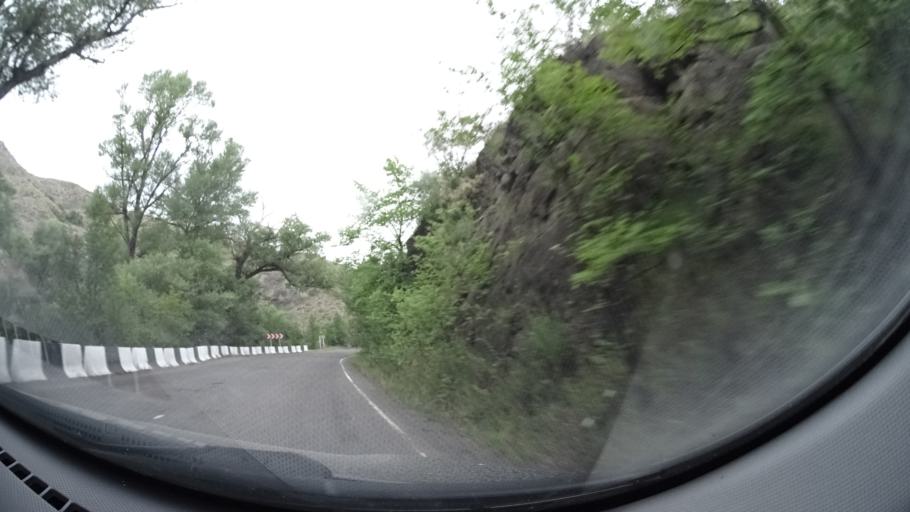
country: GE
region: Samtskhe-Javakheti
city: Akhaltsikhe
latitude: 41.6166
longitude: 43.0656
